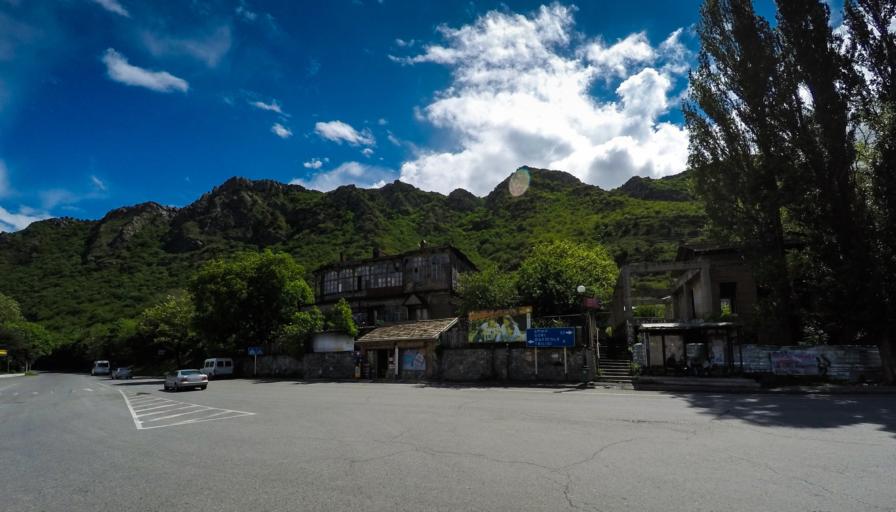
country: GE
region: Mtskheta-Mtianeti
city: Mtskheta
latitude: 41.8383
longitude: 44.7040
